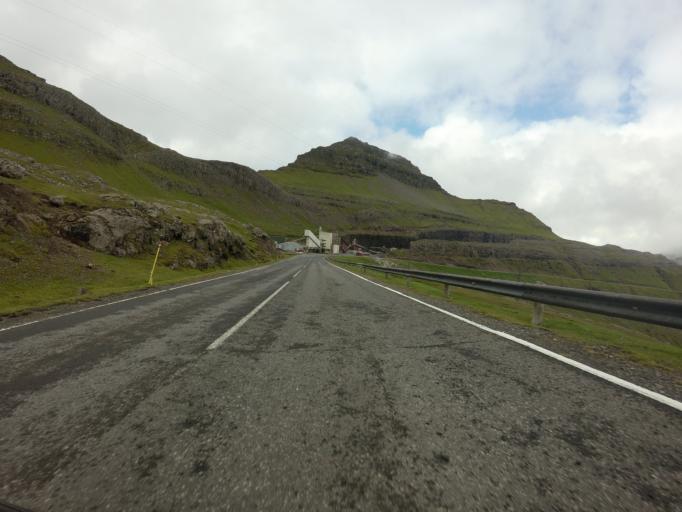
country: FO
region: Streymoy
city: Kollafjordhur
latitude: 62.0905
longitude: -6.9614
